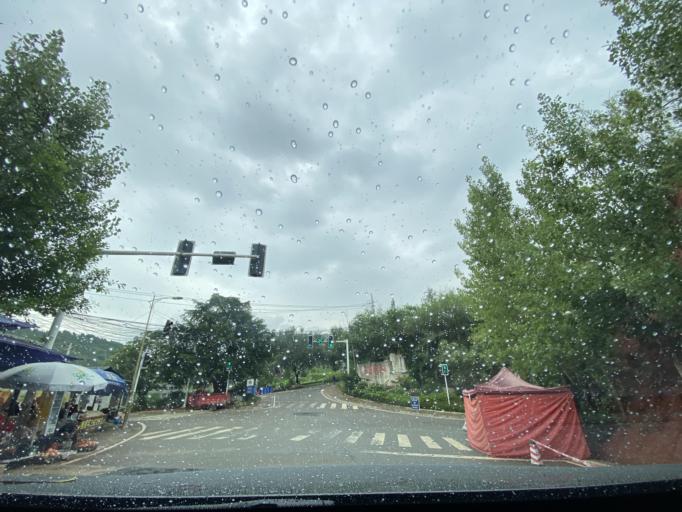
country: CN
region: Sichuan
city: Longquan
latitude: 30.6071
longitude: 104.4756
